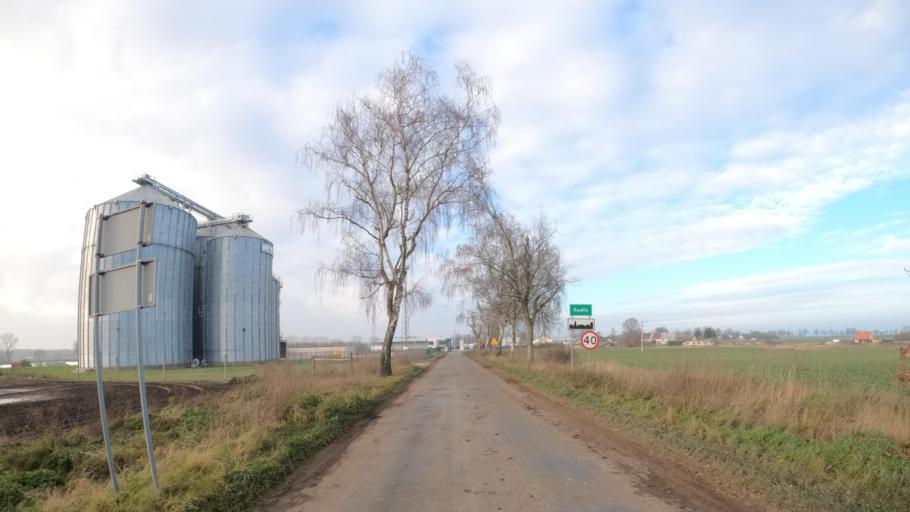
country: PL
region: West Pomeranian Voivodeship
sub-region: Powiat goleniowski
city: Osina
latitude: 53.5802
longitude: 15.0848
